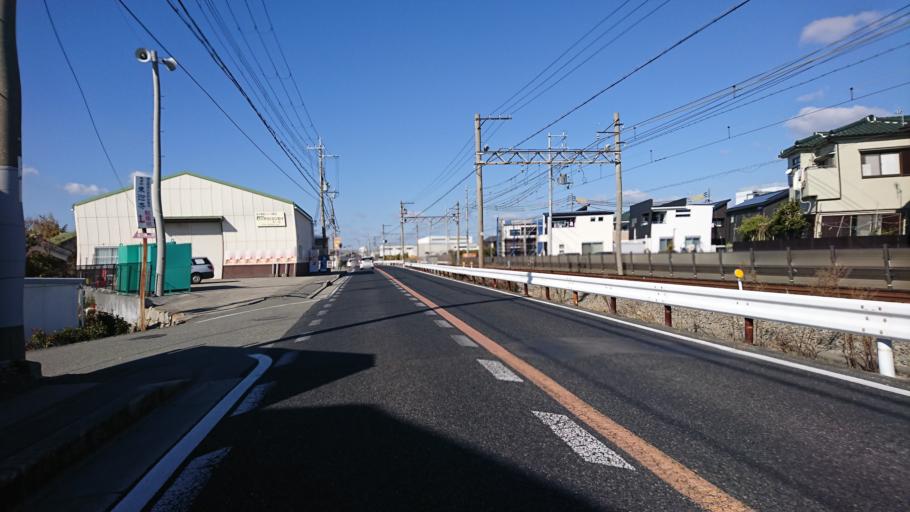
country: JP
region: Hyogo
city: Akashi
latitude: 34.6726
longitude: 134.9335
